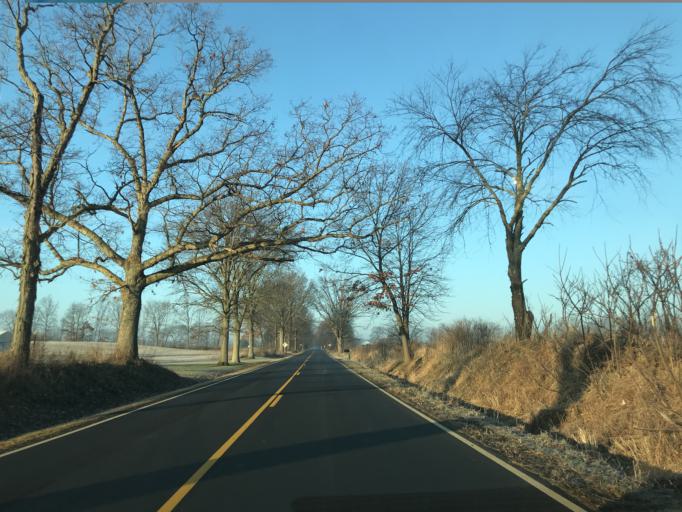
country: US
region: Michigan
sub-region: Ingham County
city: Leslie
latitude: 42.4221
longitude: -84.5192
